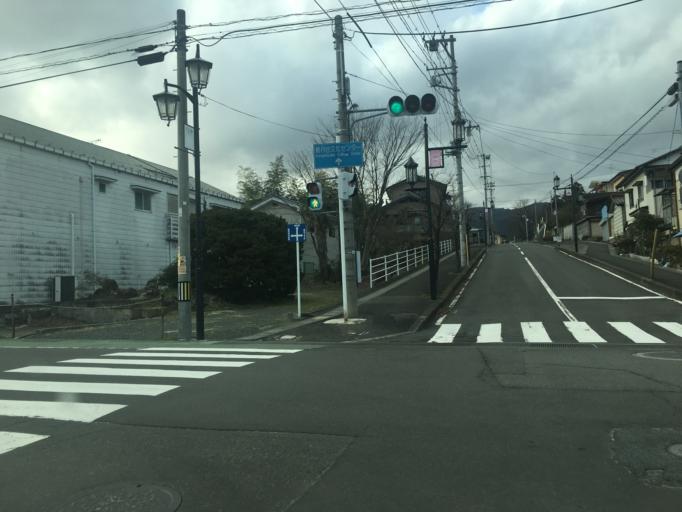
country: JP
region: Fukushima
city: Hobaramachi
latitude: 37.8766
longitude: 140.5457
